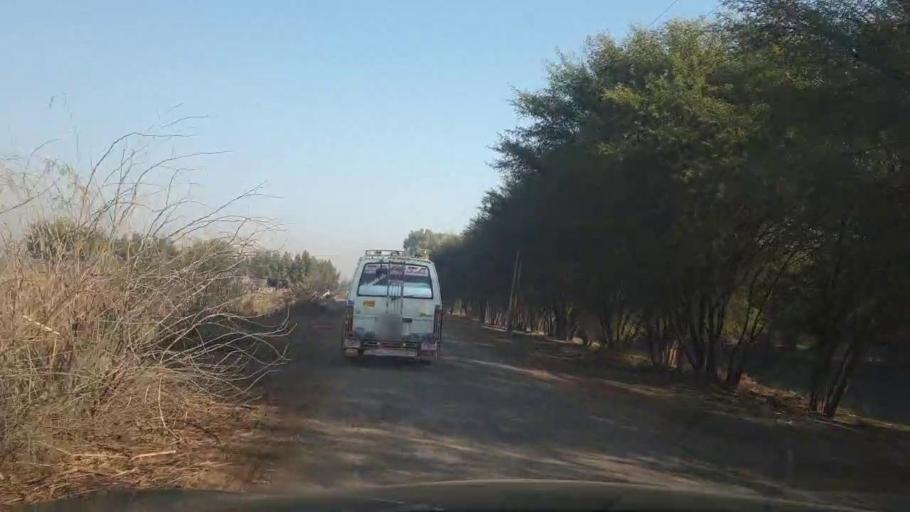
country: PK
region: Sindh
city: Mirpur Mathelo
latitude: 28.0690
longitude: 69.4664
